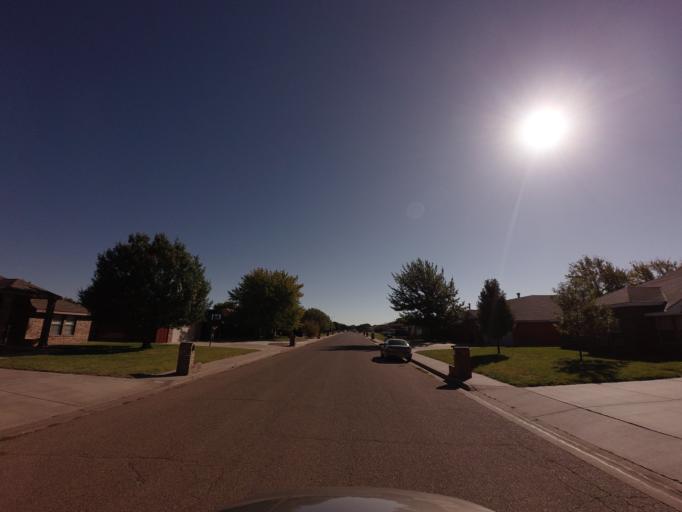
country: US
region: New Mexico
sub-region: Curry County
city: Clovis
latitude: 34.4289
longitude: -103.1736
